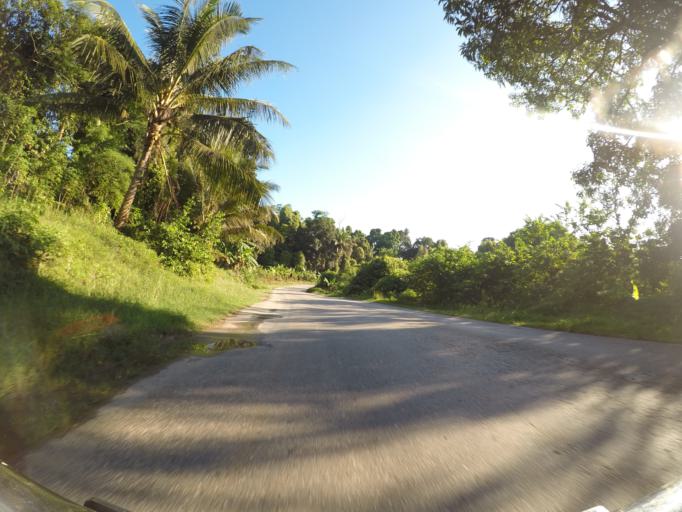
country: TZ
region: Pemba South
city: Mtambile
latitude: -5.3737
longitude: 39.7052
